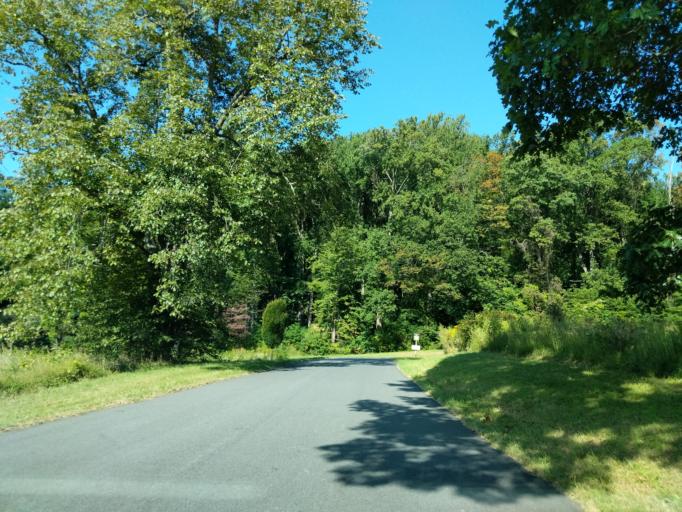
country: US
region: Pennsylvania
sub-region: Chester County
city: Chesterbrook
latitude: 40.0903
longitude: -75.4480
